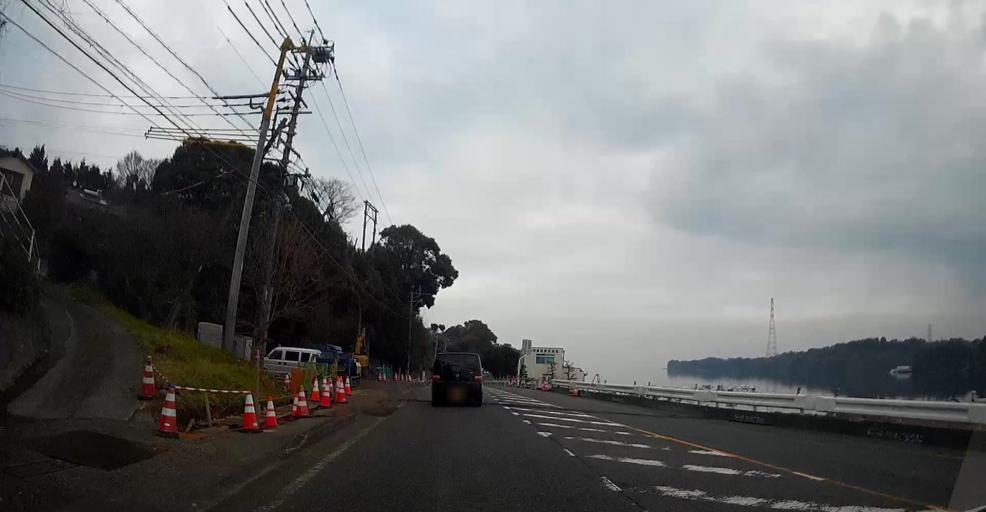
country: JP
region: Kumamoto
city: Yatsushiro
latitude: 32.6125
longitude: 130.4937
